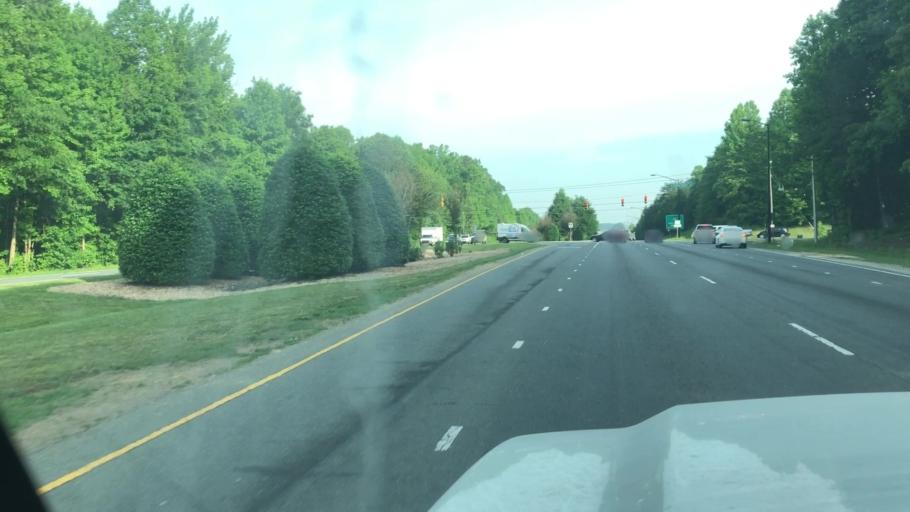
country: US
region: North Carolina
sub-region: Gaston County
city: Mount Holly
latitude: 35.3093
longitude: -80.9250
